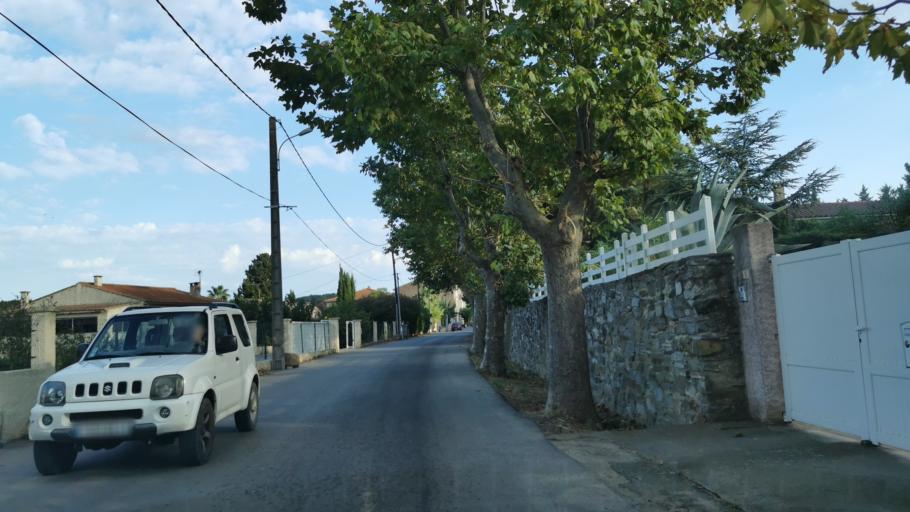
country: FR
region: Languedoc-Roussillon
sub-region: Departement de l'Aude
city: Nevian
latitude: 43.2154
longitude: 2.9012
